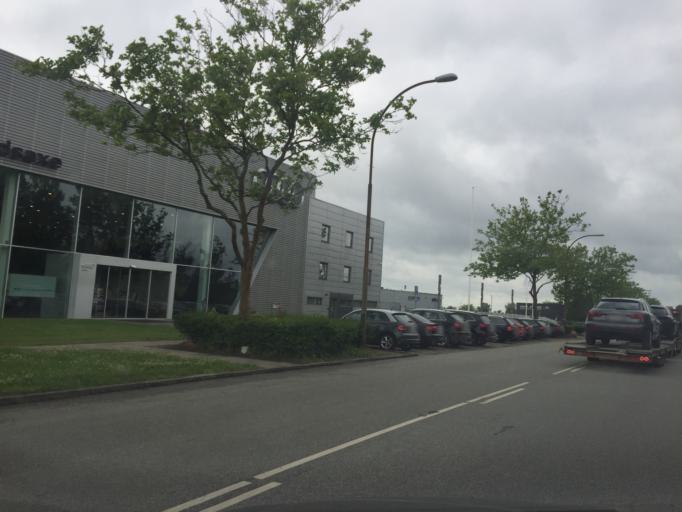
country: DK
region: Capital Region
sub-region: Herlev Kommune
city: Herlev
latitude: 55.7333
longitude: 12.4608
